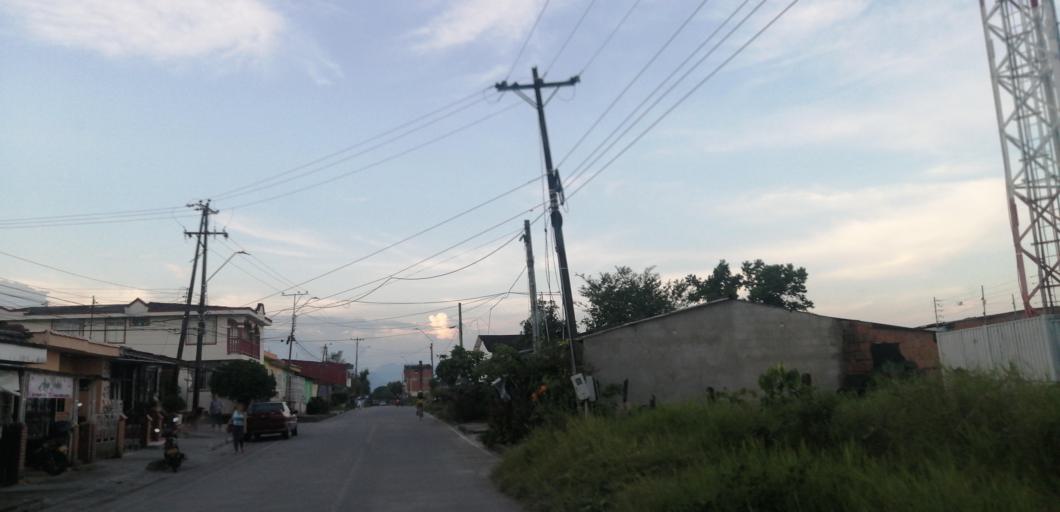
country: CO
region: Meta
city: Acacias
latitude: 3.9926
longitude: -73.7568
